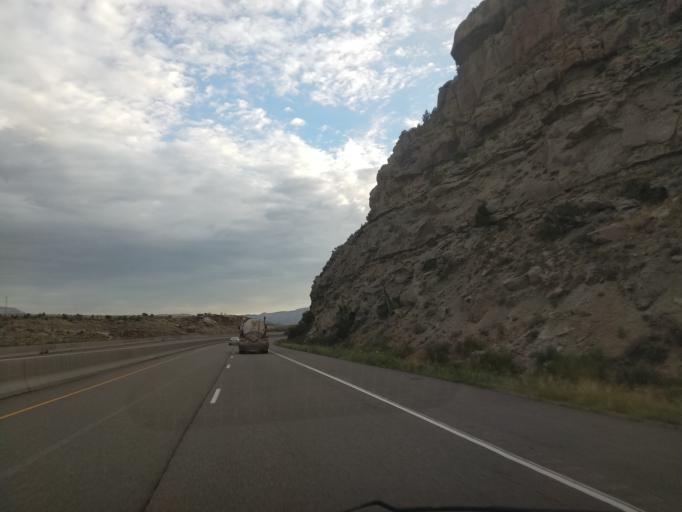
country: US
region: Colorado
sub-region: Mesa County
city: Palisade
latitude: 39.2581
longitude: -108.2594
